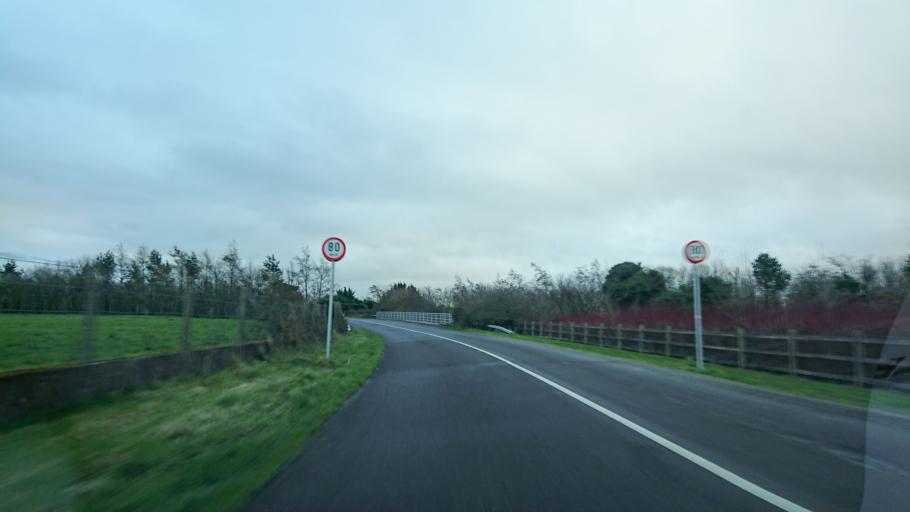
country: IE
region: Munster
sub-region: Waterford
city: Portlaw
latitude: 52.1977
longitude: -7.4272
